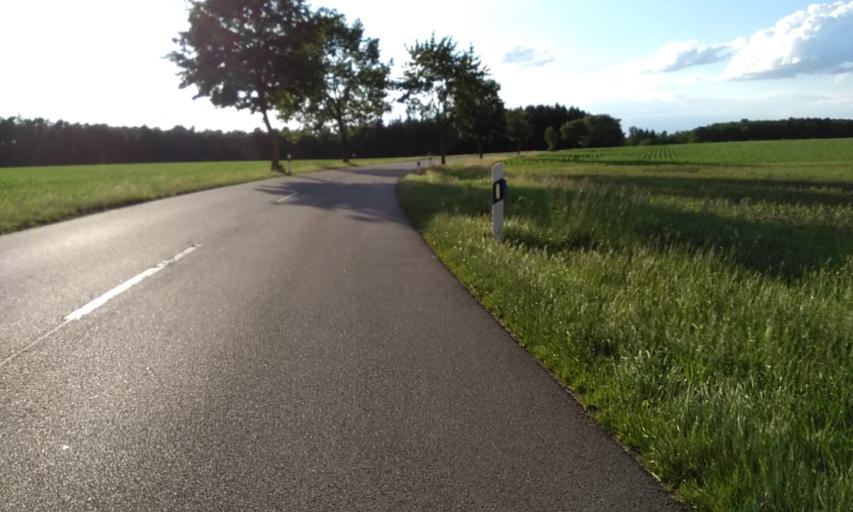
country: DE
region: Lower Saxony
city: Heeslingen
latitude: 53.3524
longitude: 9.3464
